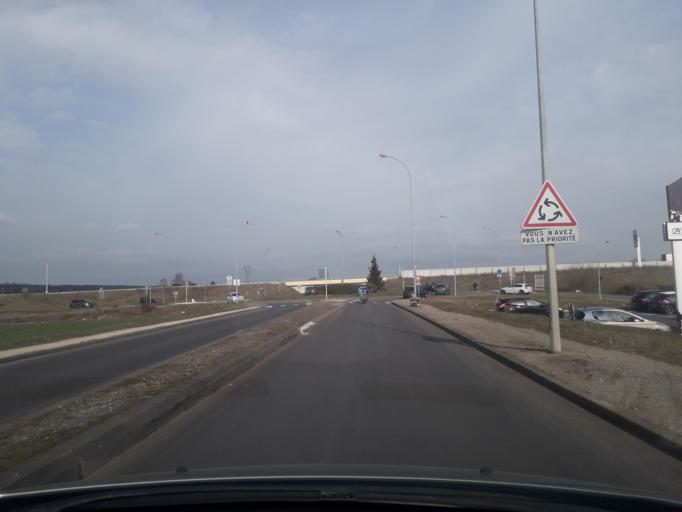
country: FR
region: Bourgogne
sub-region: Departement de la Cote-d'Or
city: Ahuy
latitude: 47.3571
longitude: 5.0343
